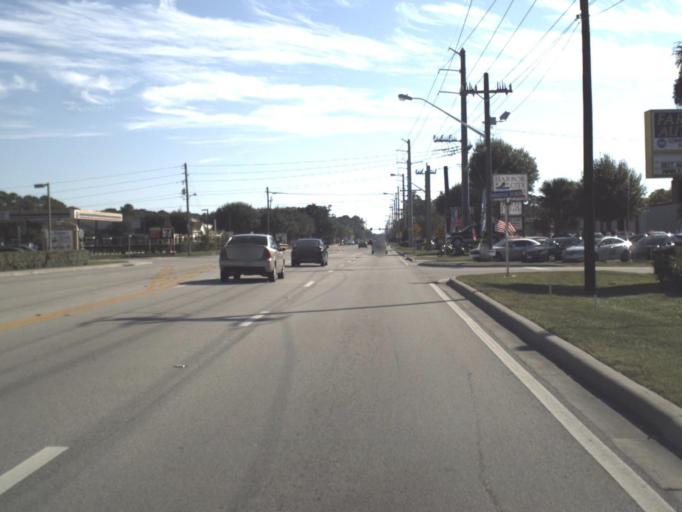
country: US
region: Florida
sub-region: Brevard County
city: June Park
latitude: 28.0988
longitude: -80.6727
